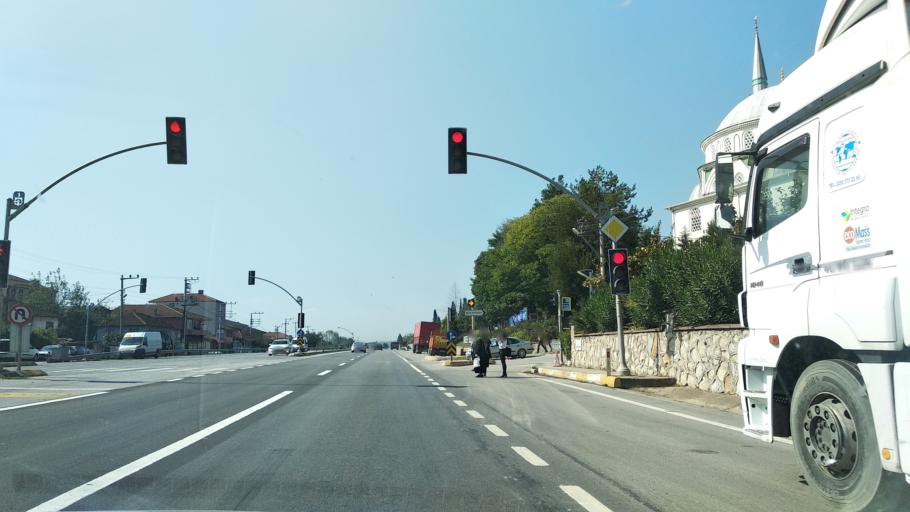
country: TR
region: Sakarya
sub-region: Merkez
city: Sapanca
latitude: 40.7338
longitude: 30.2210
